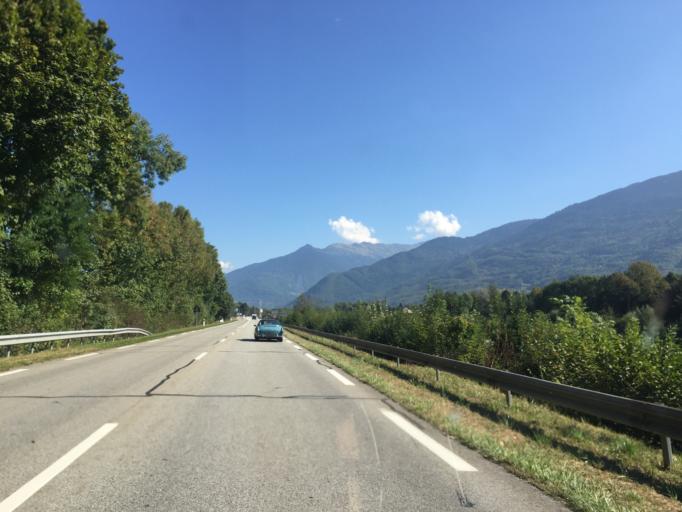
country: FR
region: Rhone-Alpes
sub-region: Departement de la Savoie
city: Frontenex
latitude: 45.6237
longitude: 6.3149
